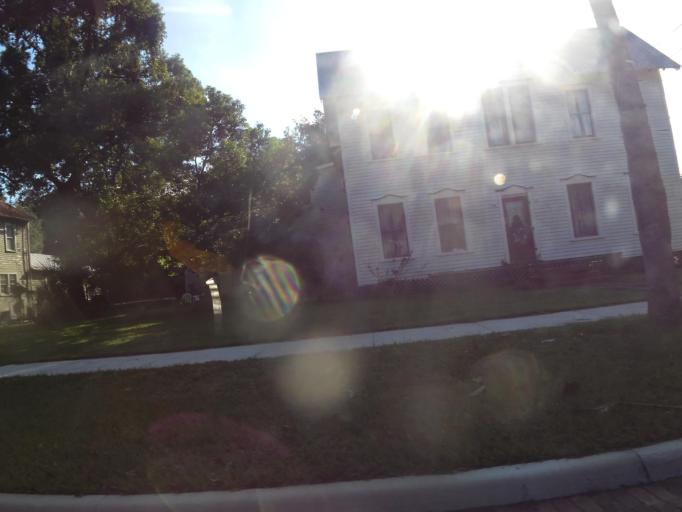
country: US
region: Florida
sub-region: Putnam County
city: Palatka
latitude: 29.6435
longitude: -81.6345
